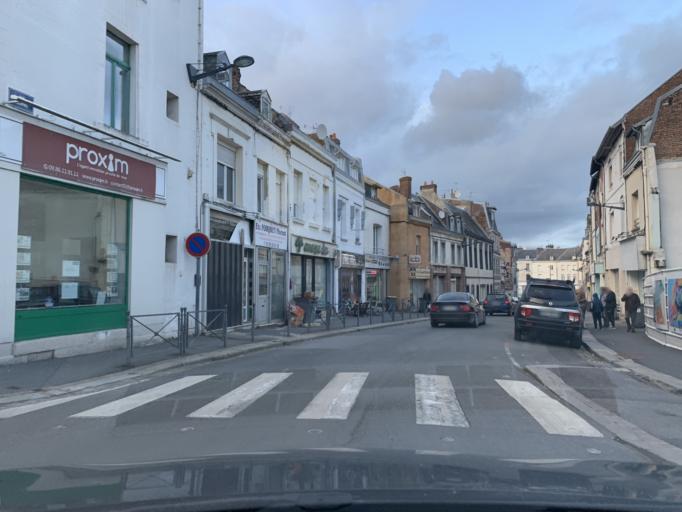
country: FR
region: Picardie
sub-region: Departement de l'Aisne
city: Saint-Quentin
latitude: 49.8500
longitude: 3.2865
